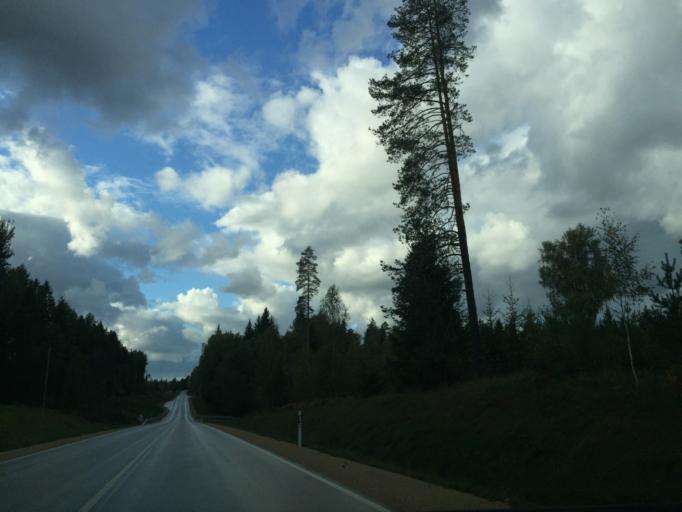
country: LV
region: Ligatne
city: Ligatne
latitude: 57.1581
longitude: 25.0621
